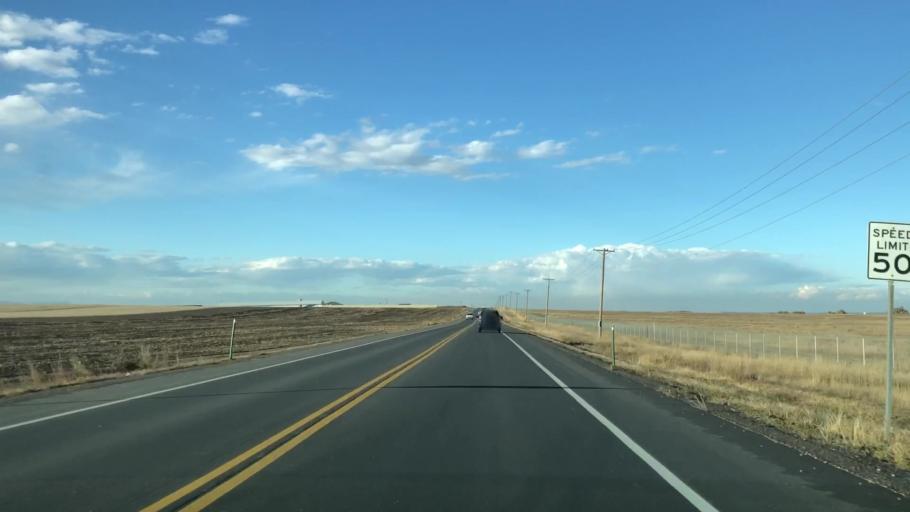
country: US
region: Colorado
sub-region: Larimer County
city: Loveland
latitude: 40.4521
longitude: -105.0205
